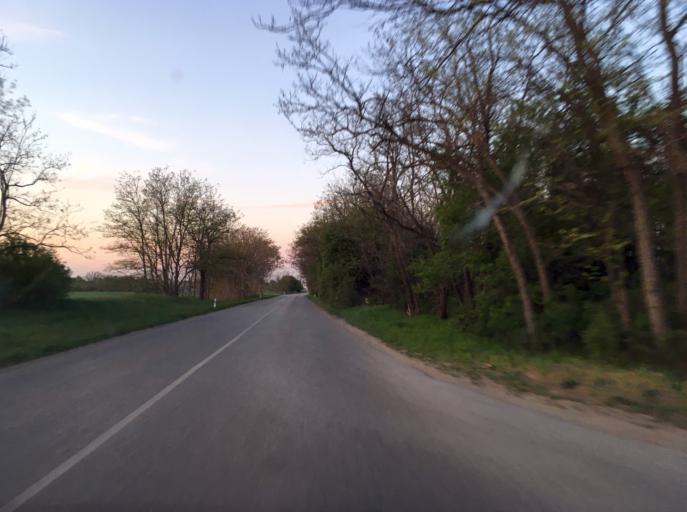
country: SK
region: Nitriansky
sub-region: Okres Nove Zamky
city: Nove Zamky
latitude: 47.9513
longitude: 18.1389
